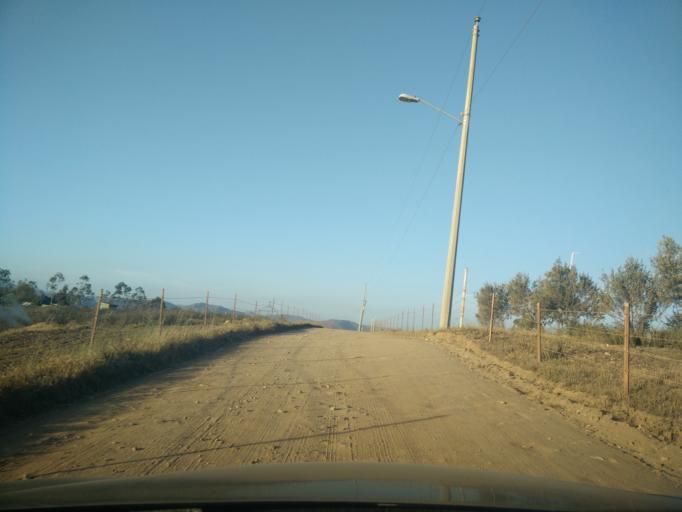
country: MX
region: Baja California
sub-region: Ensenada
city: Rancho Verde
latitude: 32.0441
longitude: -116.6516
